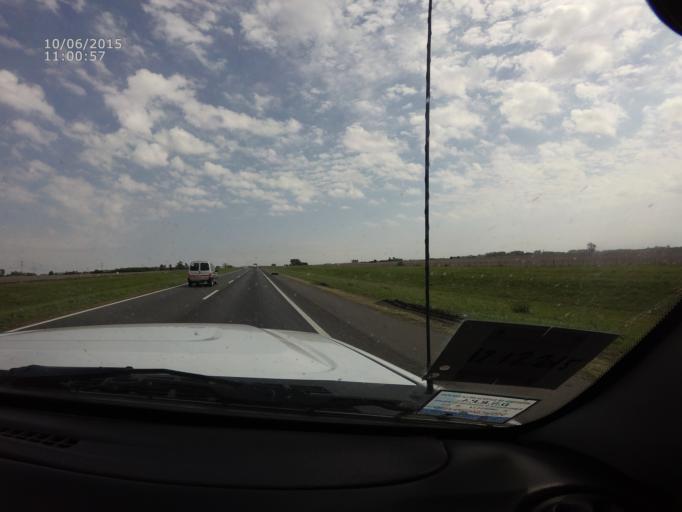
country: AR
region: Santa Fe
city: Villa Constitucion
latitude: -33.2651
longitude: -60.4083
